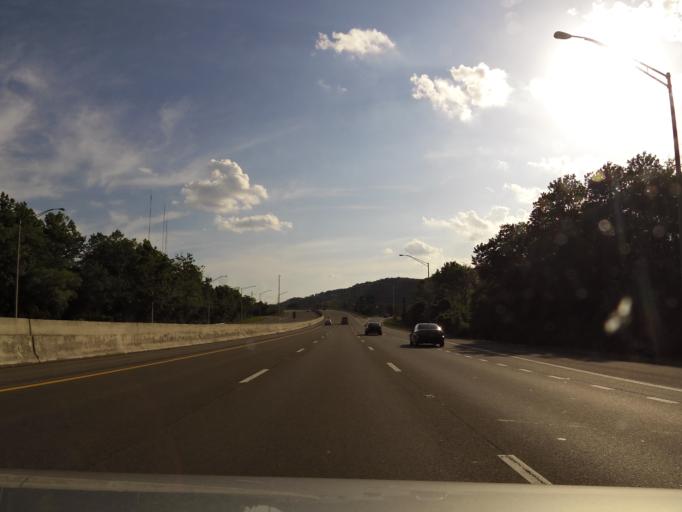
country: US
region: Tennessee
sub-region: Knox County
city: Knoxville
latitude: 36.0202
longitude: -83.9186
